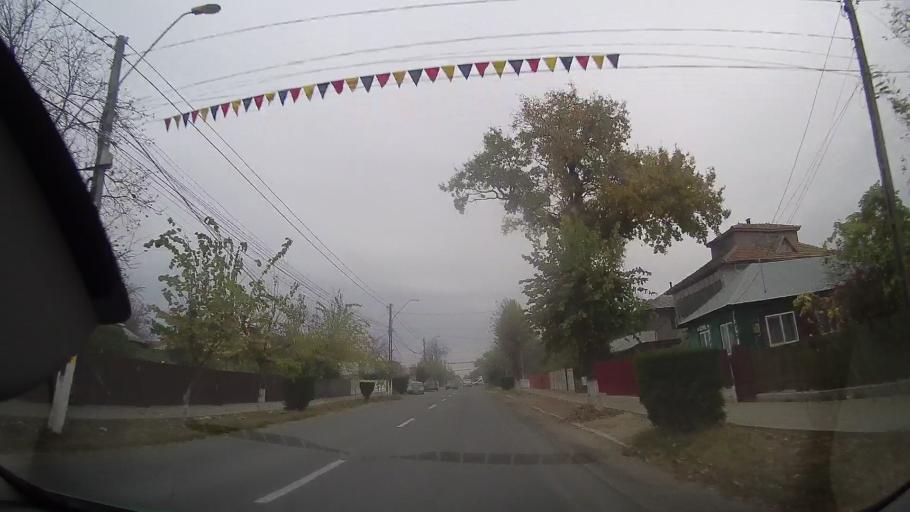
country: RO
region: Ialomita
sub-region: Oras Amara
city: Amara
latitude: 44.6157
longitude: 27.3143
